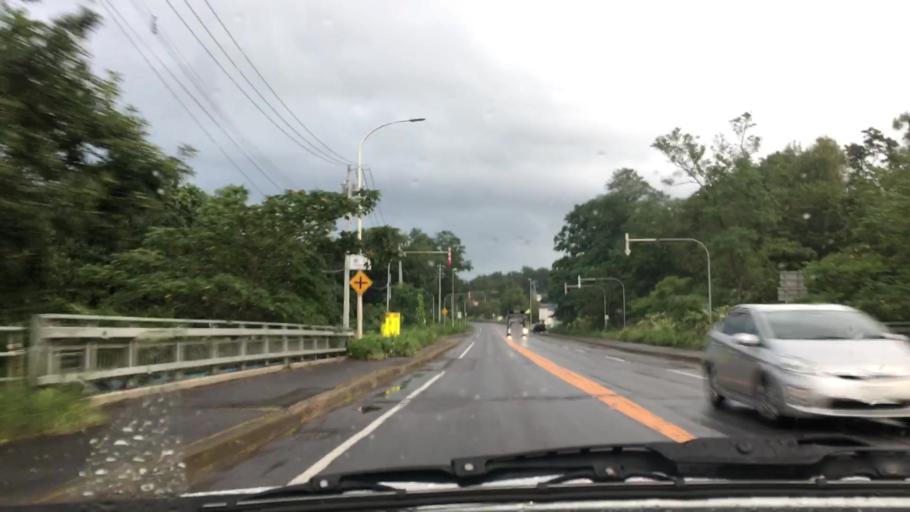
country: JP
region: Hokkaido
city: Nanae
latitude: 42.0850
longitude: 140.5849
